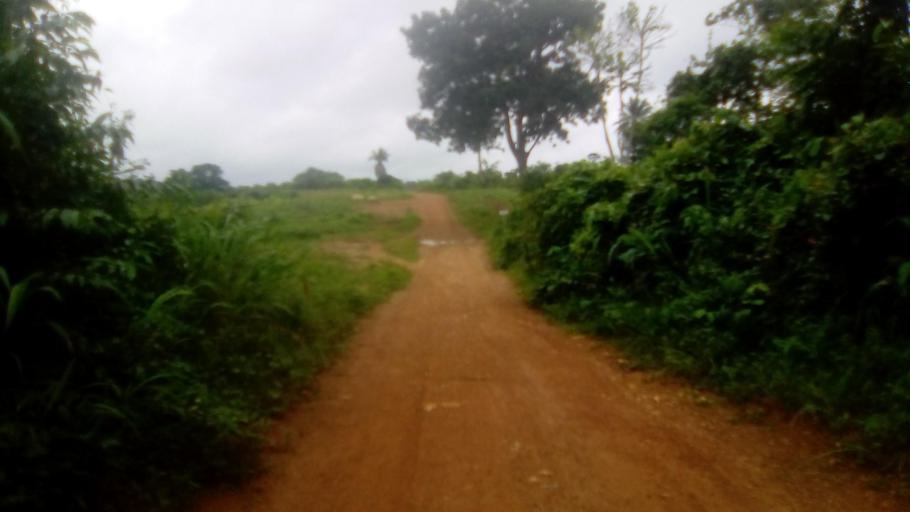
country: SL
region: Eastern Province
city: Kailahun
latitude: 8.3005
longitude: -10.5581
